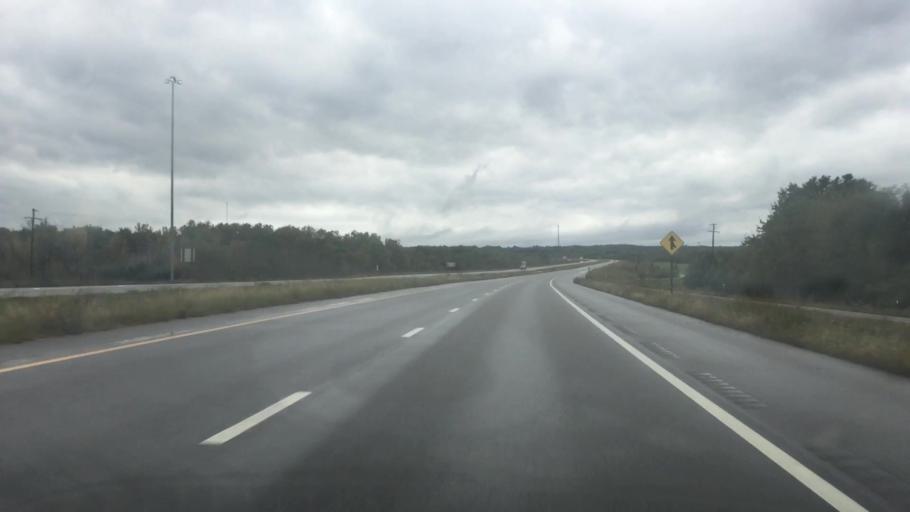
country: US
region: Kansas
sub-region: Miami County
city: Osawatomie
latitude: 38.4985
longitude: -94.9356
